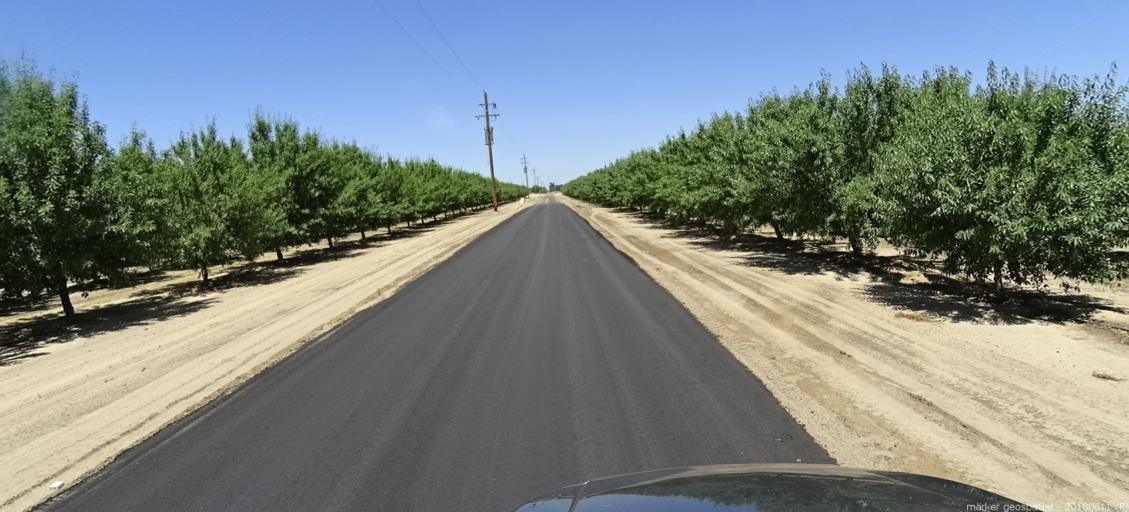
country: US
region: California
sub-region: Madera County
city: Fairmead
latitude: 37.0050
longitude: -120.1933
